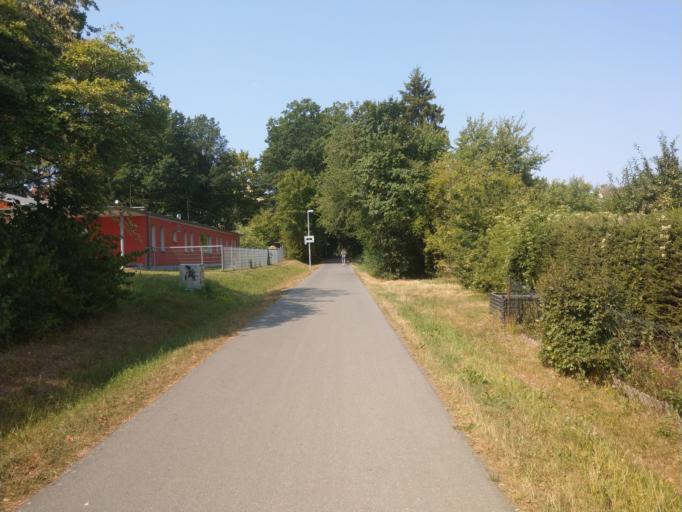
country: DE
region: Bavaria
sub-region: Upper Franconia
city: Bayreuth
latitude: 49.9307
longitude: 11.5800
